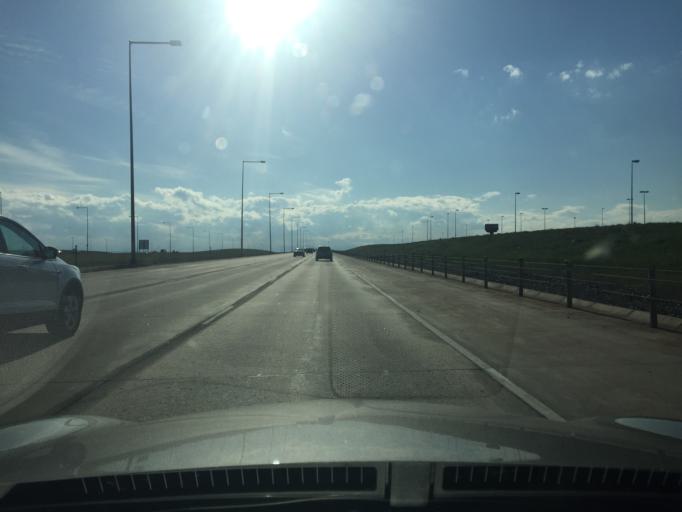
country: US
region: Colorado
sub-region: Adams County
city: Aurora
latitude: 39.8344
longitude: -104.7047
